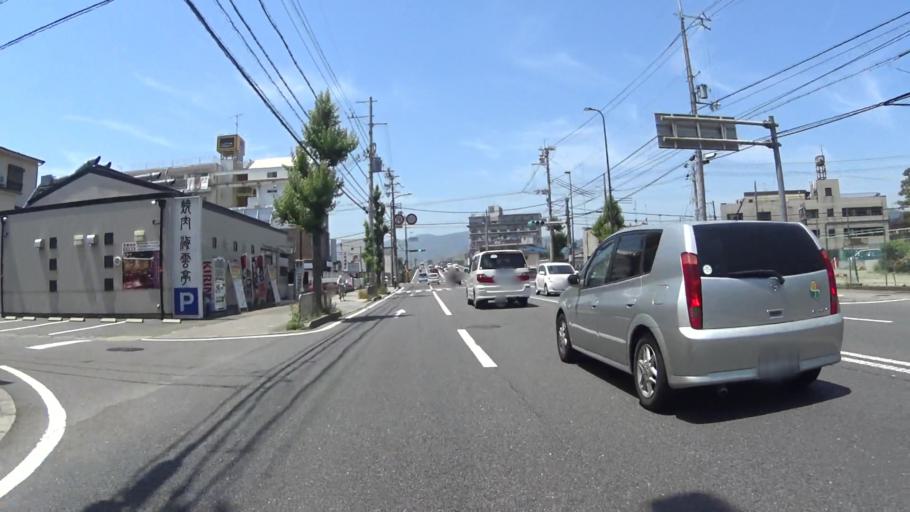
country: JP
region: Kyoto
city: Kameoka
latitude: 35.0227
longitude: 135.5592
